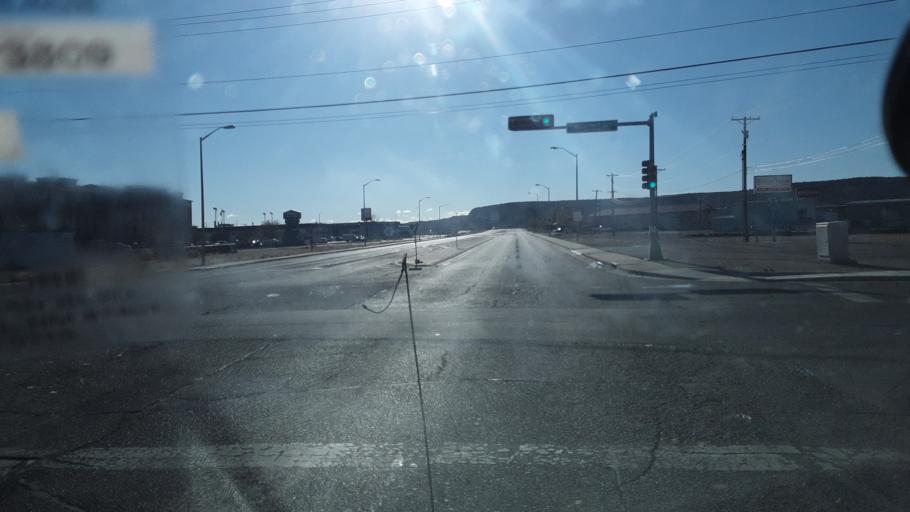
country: US
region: New Mexico
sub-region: San Juan County
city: Farmington
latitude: 36.7263
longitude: -108.1903
